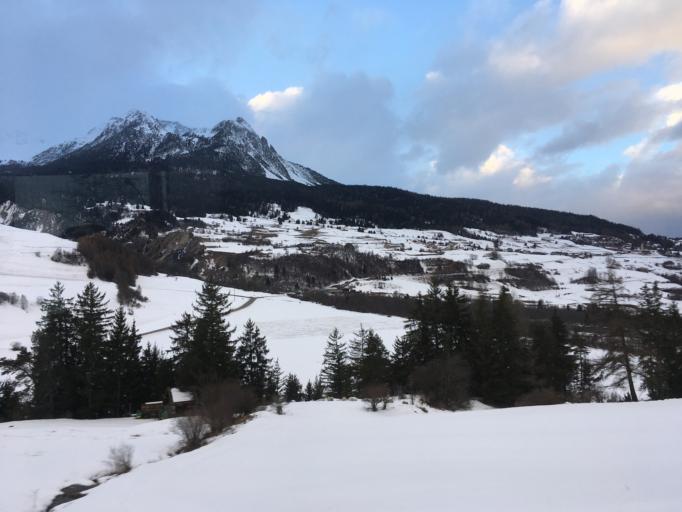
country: CH
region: Grisons
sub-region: Albula District
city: Tiefencastel
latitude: 46.6130
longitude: 9.5923
